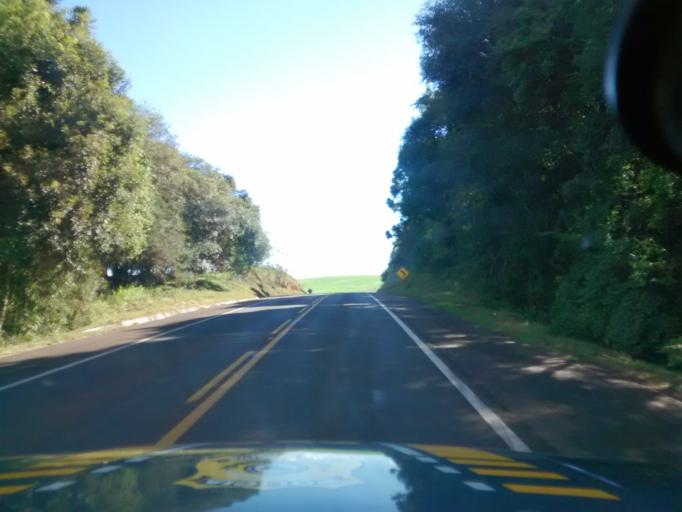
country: BR
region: Rio Grande do Sul
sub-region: Lagoa Vermelha
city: Lagoa Vermelha
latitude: -28.3296
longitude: -51.2842
